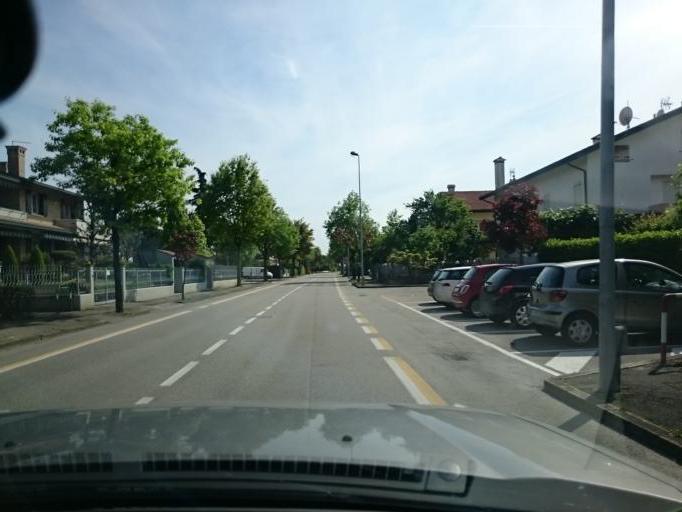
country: IT
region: Veneto
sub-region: Provincia di Padova
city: Albignasego
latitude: 45.3549
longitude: 11.8675
